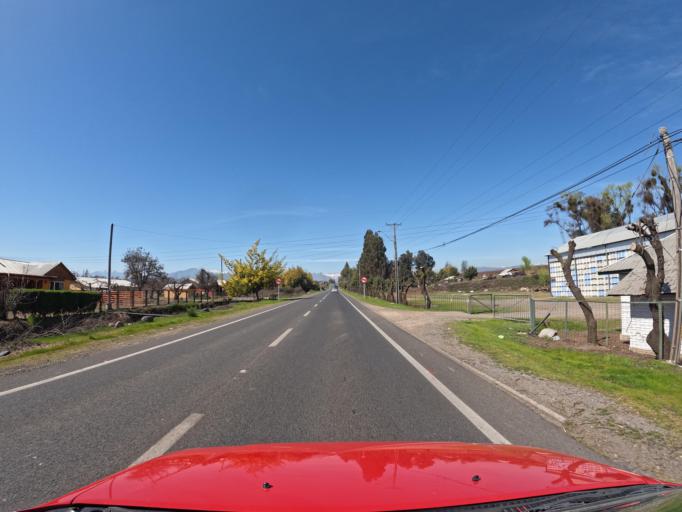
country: CL
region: Maule
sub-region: Provincia de Curico
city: Teno
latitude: -34.9628
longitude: -71.0771
